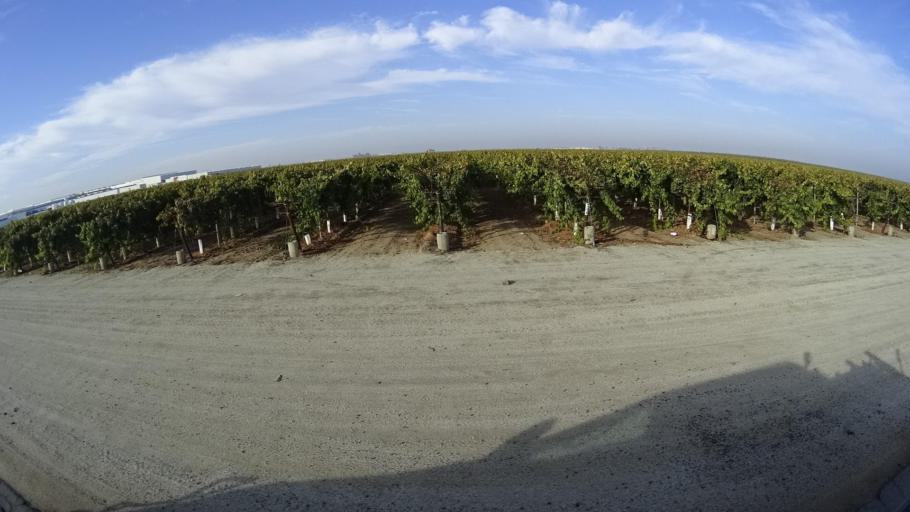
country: US
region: California
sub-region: Kern County
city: McFarland
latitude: 35.7075
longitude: -119.2050
